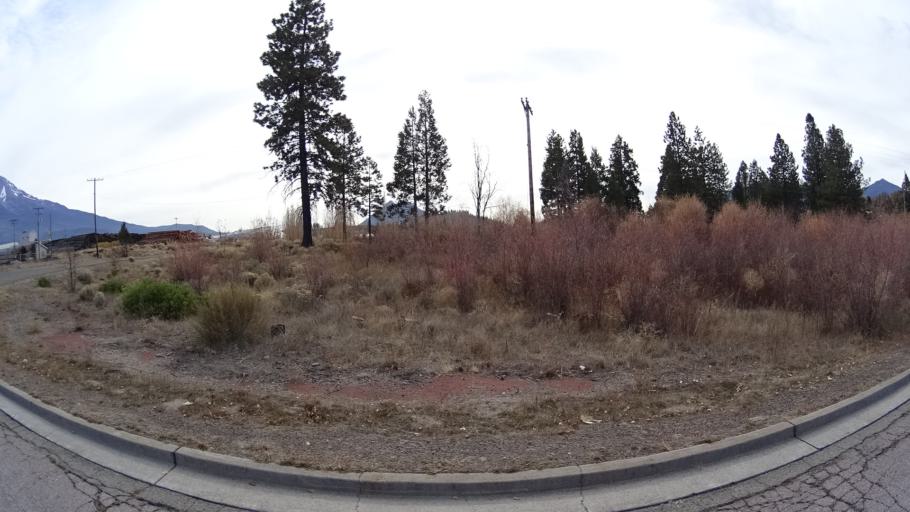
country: US
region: California
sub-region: Siskiyou County
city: Weed
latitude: 41.4362
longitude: -122.3839
